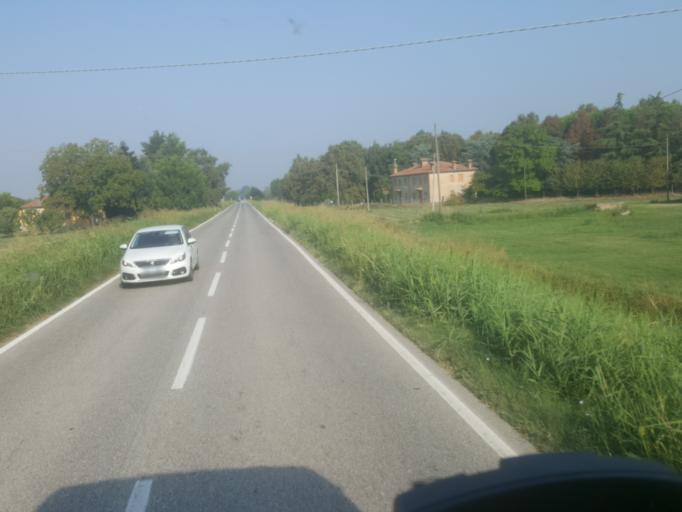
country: IT
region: Emilia-Romagna
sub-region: Provincia di Ravenna
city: Lavezzola
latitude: 44.5670
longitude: 11.8959
